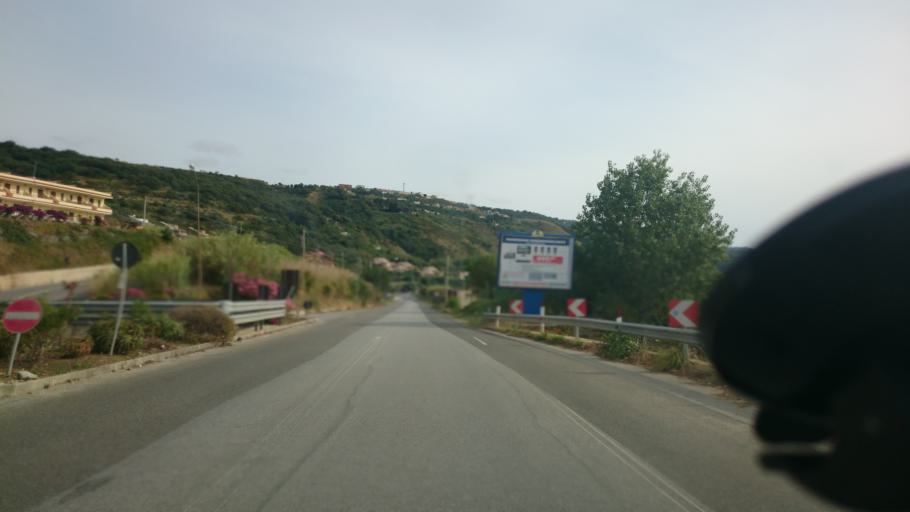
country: IT
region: Calabria
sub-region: Provincia di Vibo-Valentia
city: Zambrone
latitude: 38.7116
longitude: 15.9763
